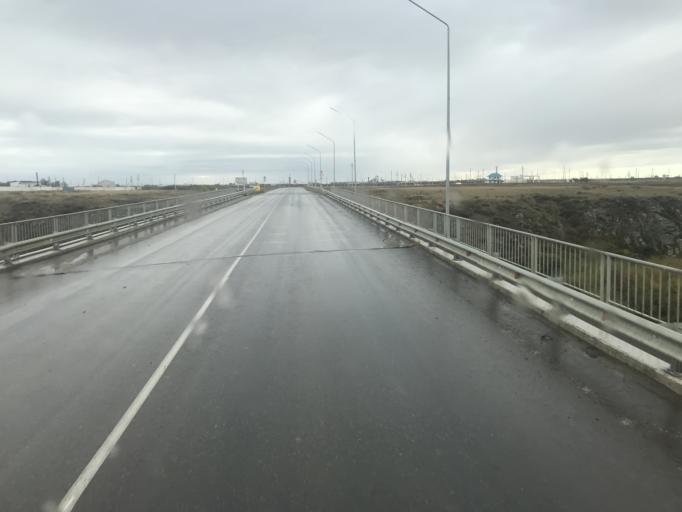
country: KZ
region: Qostanay
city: Ordzhonikidze
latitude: 52.4601
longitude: 61.7348
